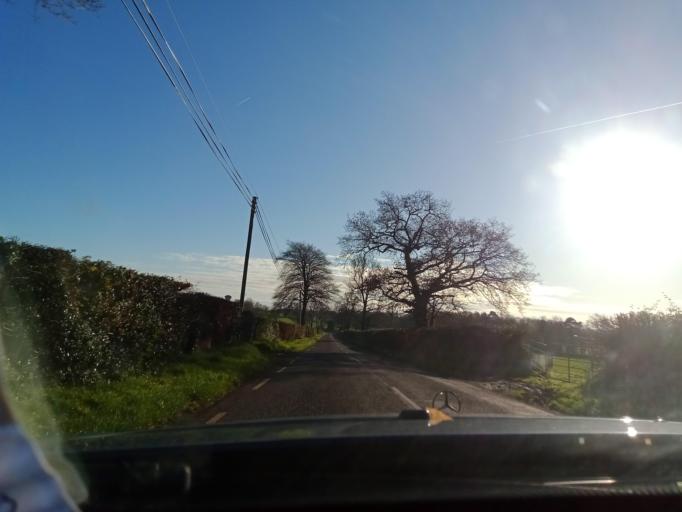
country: IE
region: Leinster
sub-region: Kilkenny
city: Piltown
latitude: 52.3646
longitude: -7.3294
